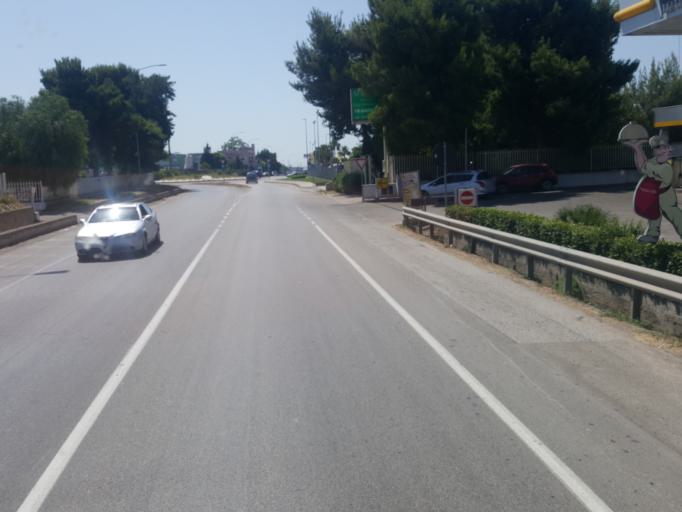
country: IT
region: Apulia
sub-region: Provincia di Taranto
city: Massafra
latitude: 40.5837
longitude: 17.1108
